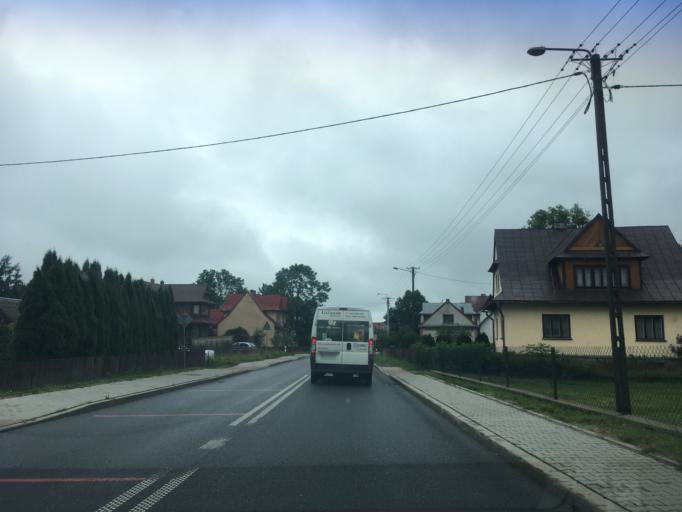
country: PL
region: Lesser Poland Voivodeship
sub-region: Powiat nowotarski
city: Czarny Dunajec
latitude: 49.4035
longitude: 19.8232
